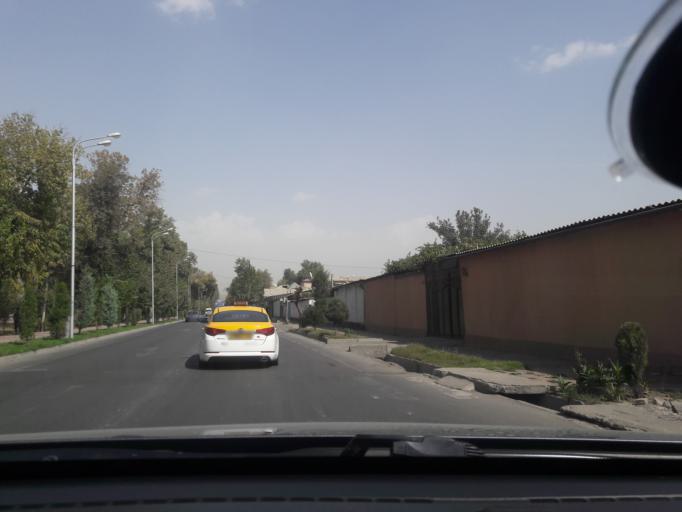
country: TJ
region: Dushanbe
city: Dushanbe
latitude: 38.5642
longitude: 68.7624
